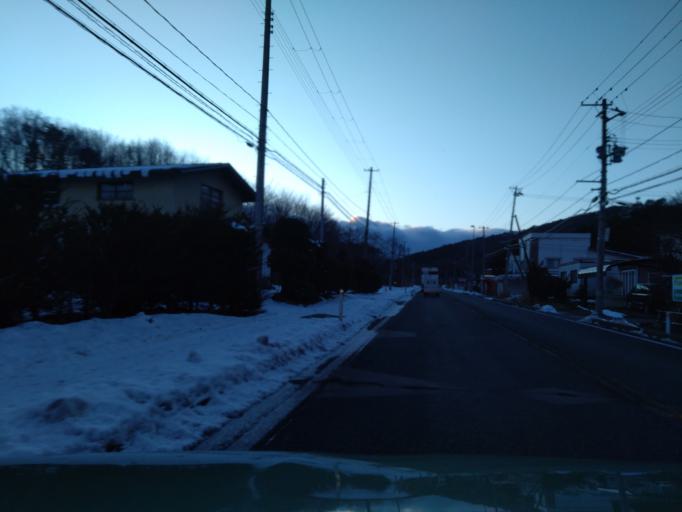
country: JP
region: Iwate
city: Shizukuishi
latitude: 39.6917
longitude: 141.0100
